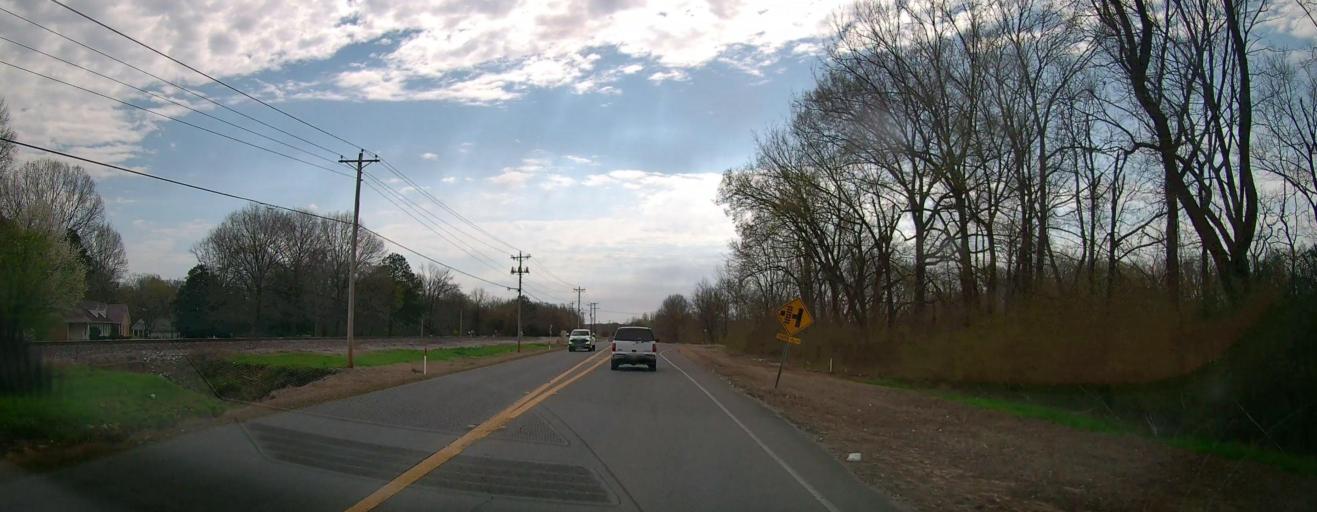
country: US
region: Mississippi
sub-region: De Soto County
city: Olive Branch
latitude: 34.9184
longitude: -89.7691
